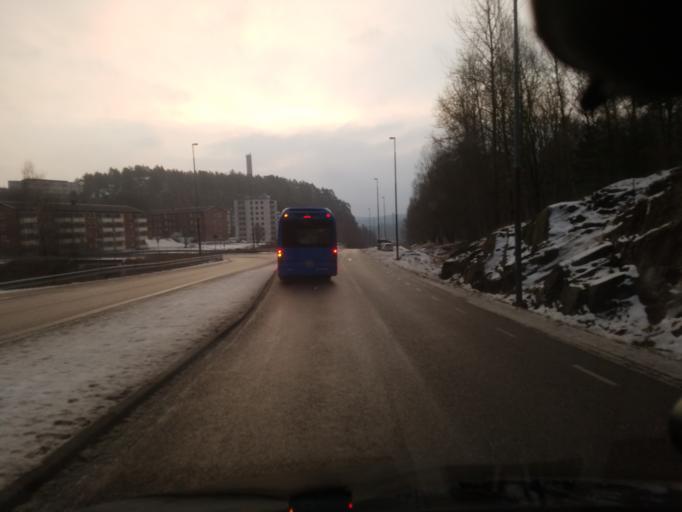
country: SE
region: Vaestra Goetaland
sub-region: Uddevalla Kommun
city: Uddevalla
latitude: 58.3607
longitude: 11.9046
